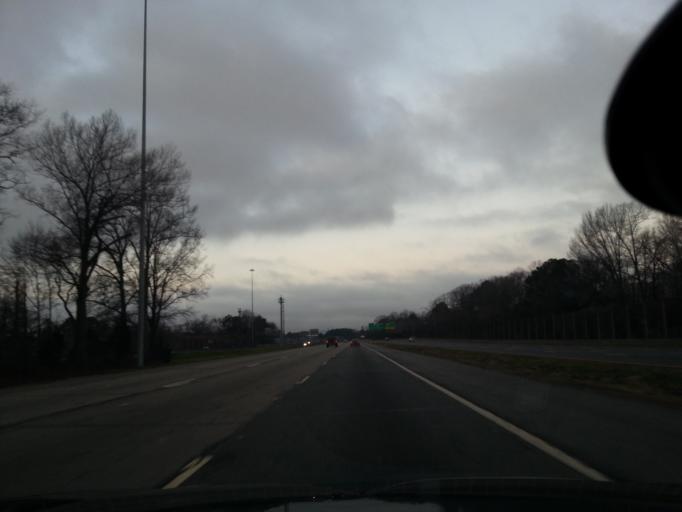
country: US
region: Virginia
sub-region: City of Chesapeake
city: Chesapeake
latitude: 36.8454
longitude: -76.2019
